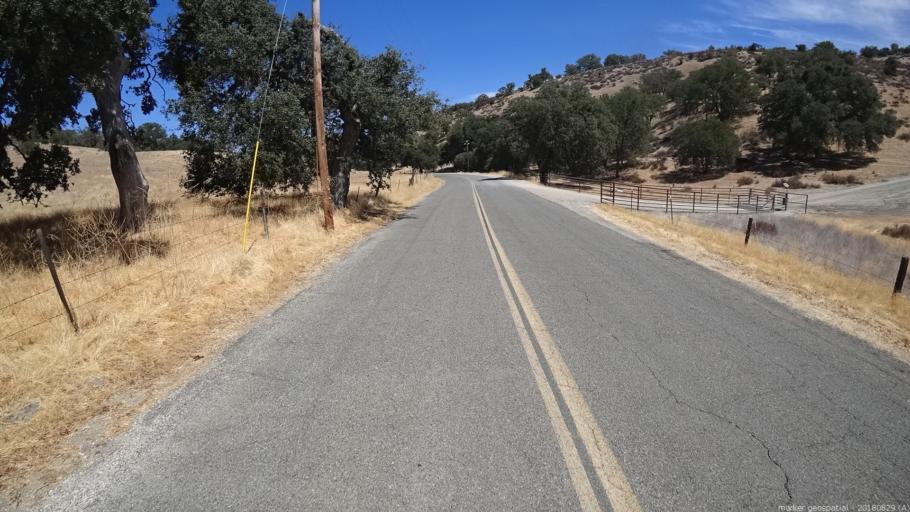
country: US
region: California
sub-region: San Luis Obispo County
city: Lake Nacimiento
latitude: 35.8869
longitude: -120.9917
